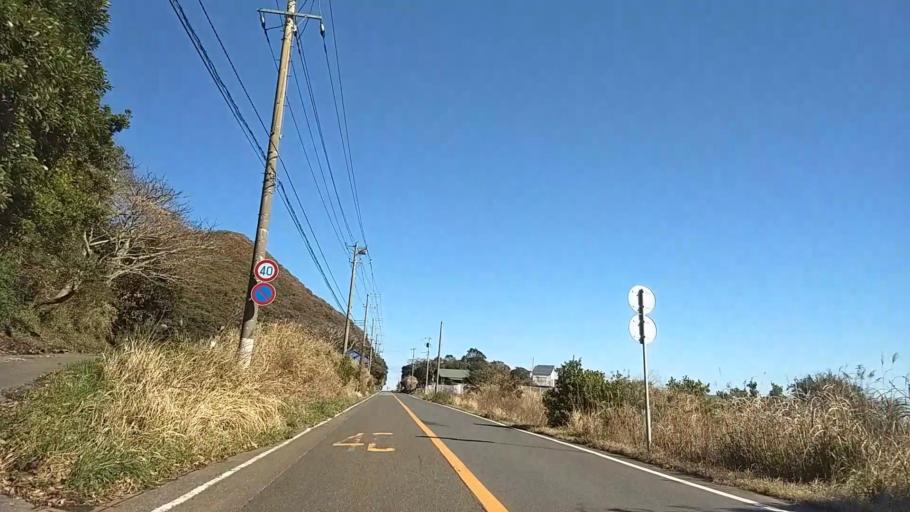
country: JP
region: Chiba
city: Tateyama
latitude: 34.9153
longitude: 139.9322
